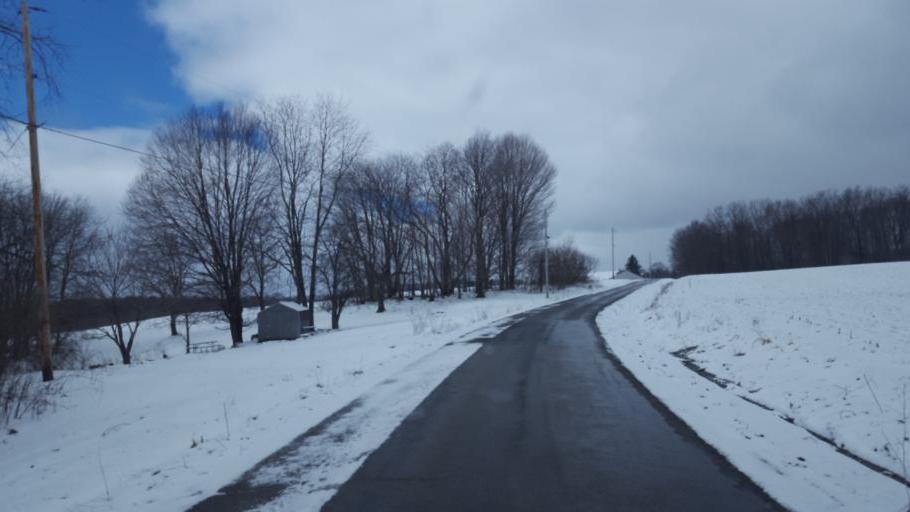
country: US
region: Pennsylvania
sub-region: Mercer County
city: Stoneboro
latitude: 41.4071
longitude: -80.0959
